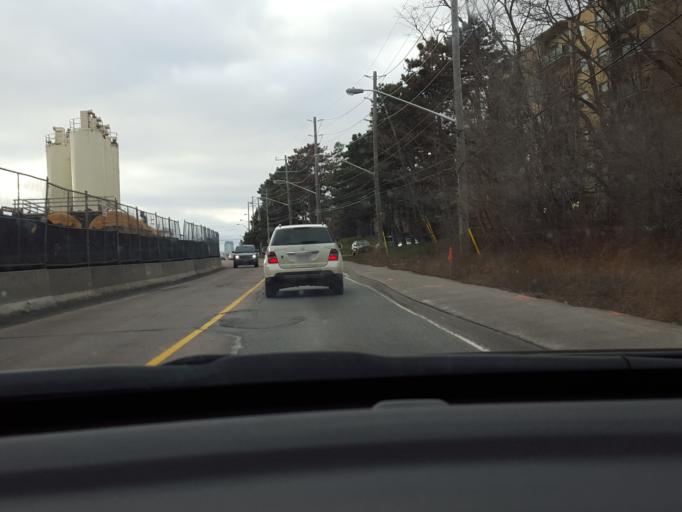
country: CA
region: Ontario
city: Toronto
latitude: 43.7154
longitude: -79.3568
